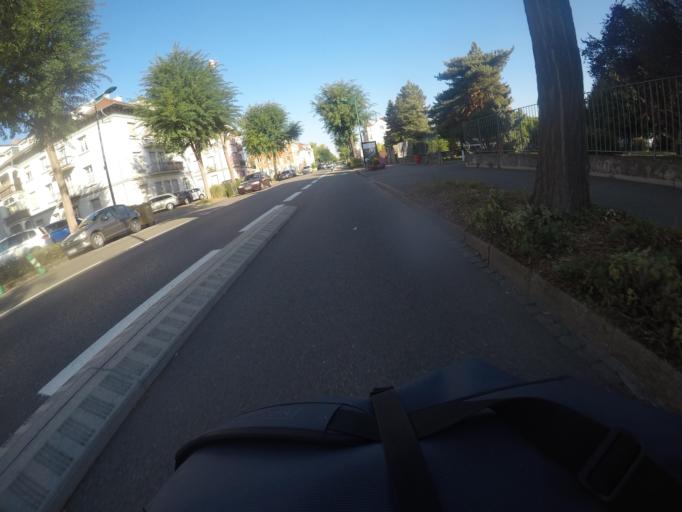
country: FR
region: Alsace
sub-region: Departement du Haut-Rhin
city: Village-Neuf
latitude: 47.5788
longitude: 7.5705
